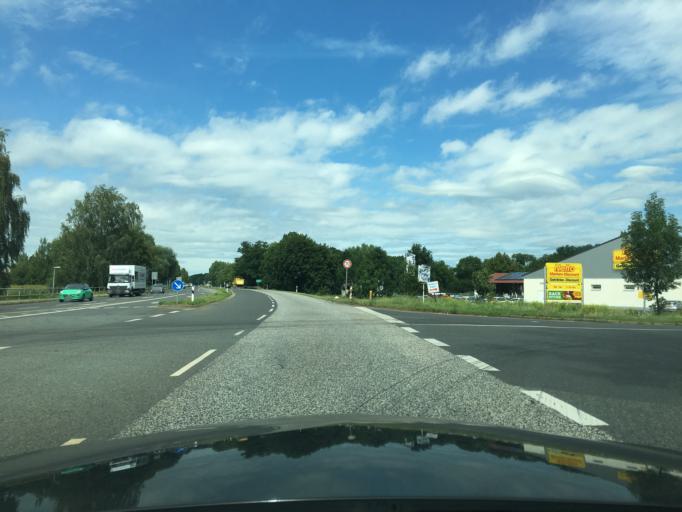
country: DE
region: Brandenburg
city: Oranienburg
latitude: 52.8129
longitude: 13.2231
